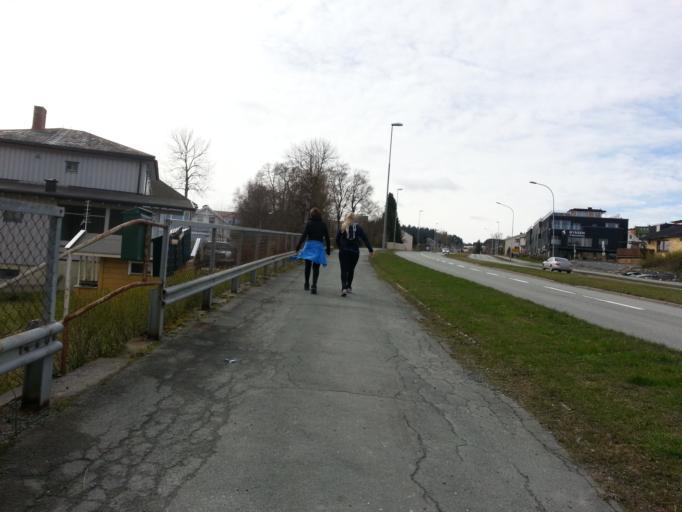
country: NO
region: Sor-Trondelag
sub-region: Trondheim
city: Trondheim
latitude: 63.4168
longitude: 10.3714
